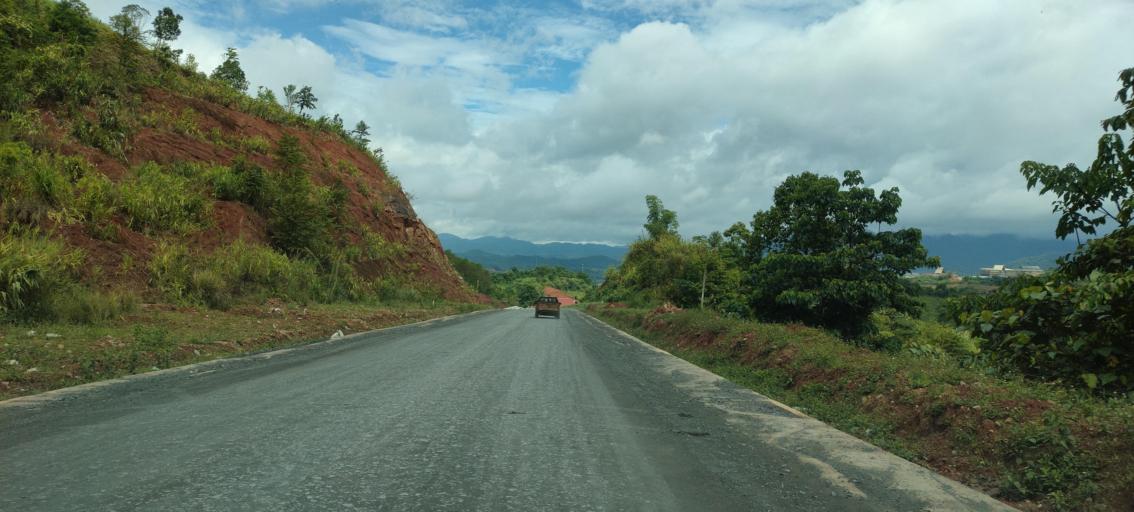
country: LA
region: Phongsali
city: Phongsali
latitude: 21.6314
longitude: 101.9268
